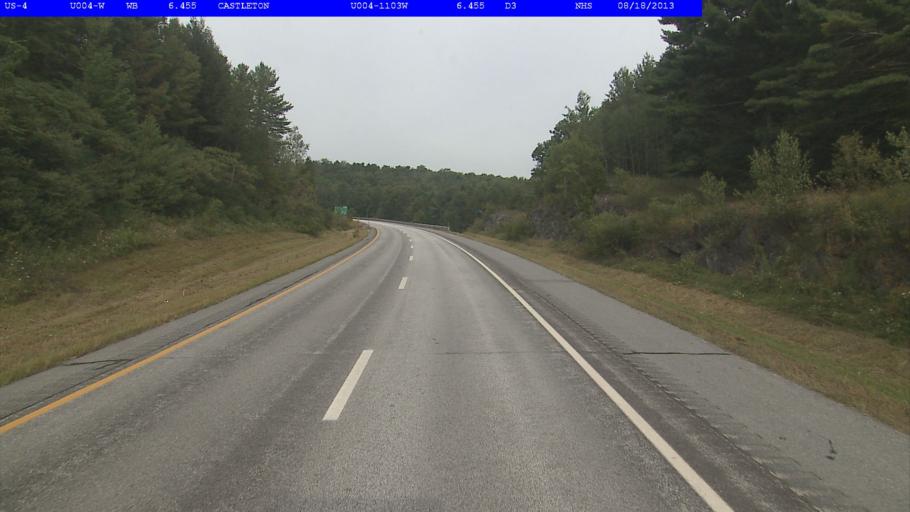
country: US
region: Vermont
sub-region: Rutland County
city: Castleton
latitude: 43.6230
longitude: -73.1889
